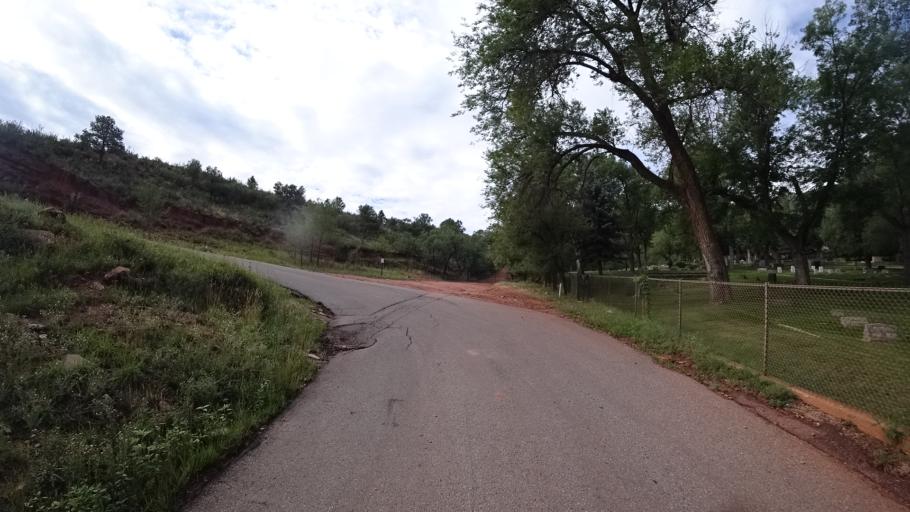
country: US
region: Colorado
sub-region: El Paso County
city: Manitou Springs
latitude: 38.8527
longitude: -104.9027
